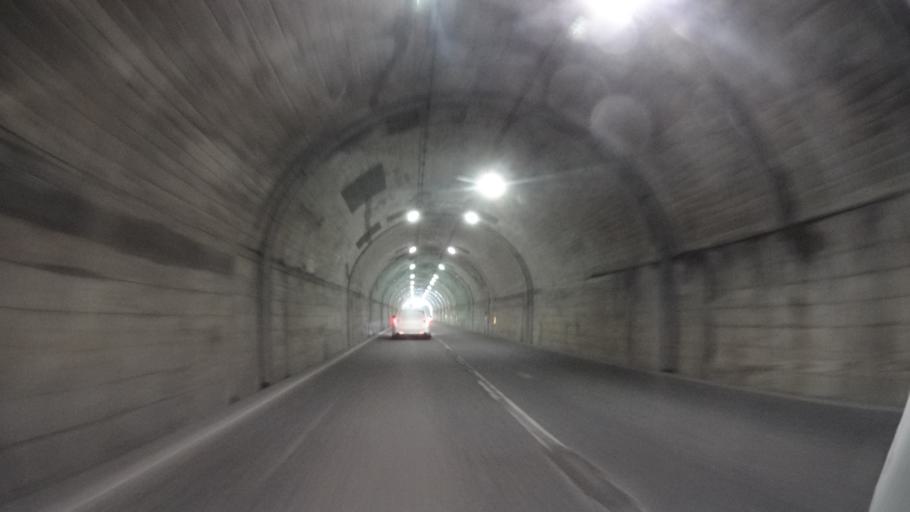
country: JP
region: Fukui
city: Ono
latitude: 35.8902
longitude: 136.6918
